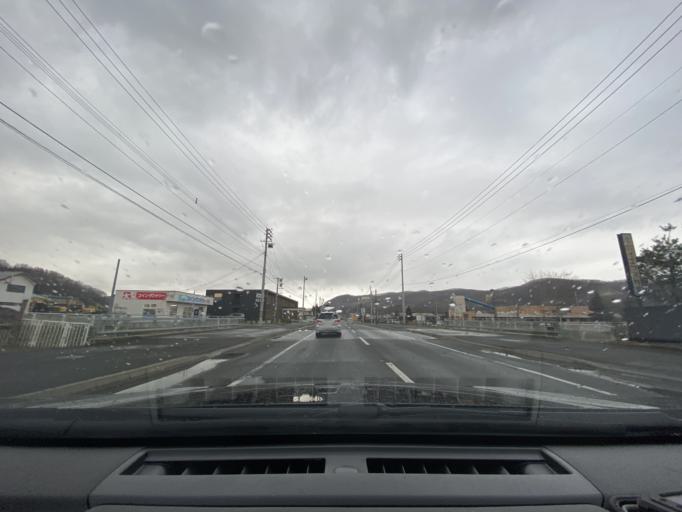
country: JP
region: Hokkaido
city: Otofuke
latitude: 43.2471
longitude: 143.5472
